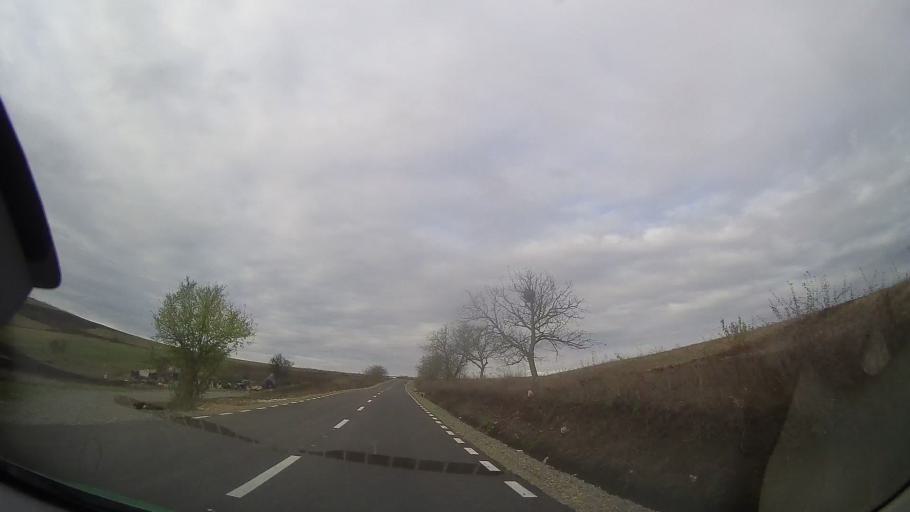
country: RO
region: Bistrita-Nasaud
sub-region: Comuna Teaca
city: Ocnita
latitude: 46.8263
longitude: 24.4774
